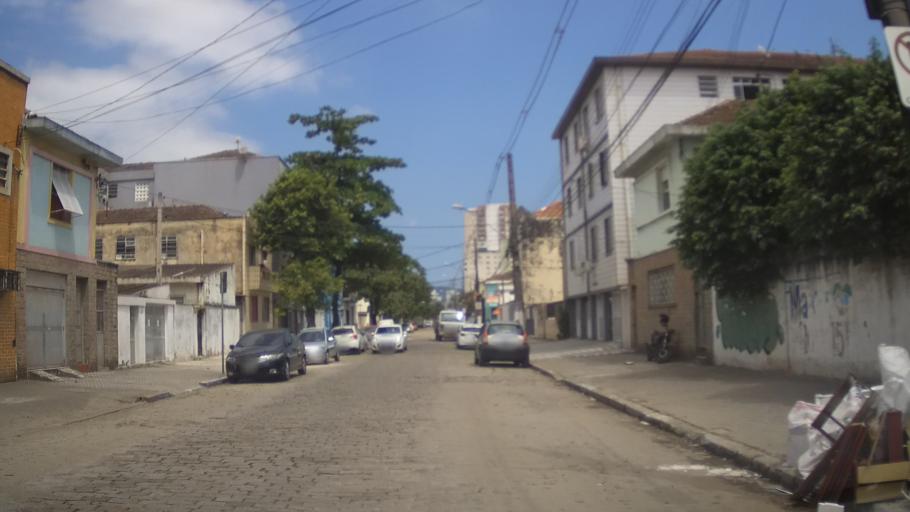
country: BR
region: Sao Paulo
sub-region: Santos
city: Santos
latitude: -23.9579
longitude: -46.3111
